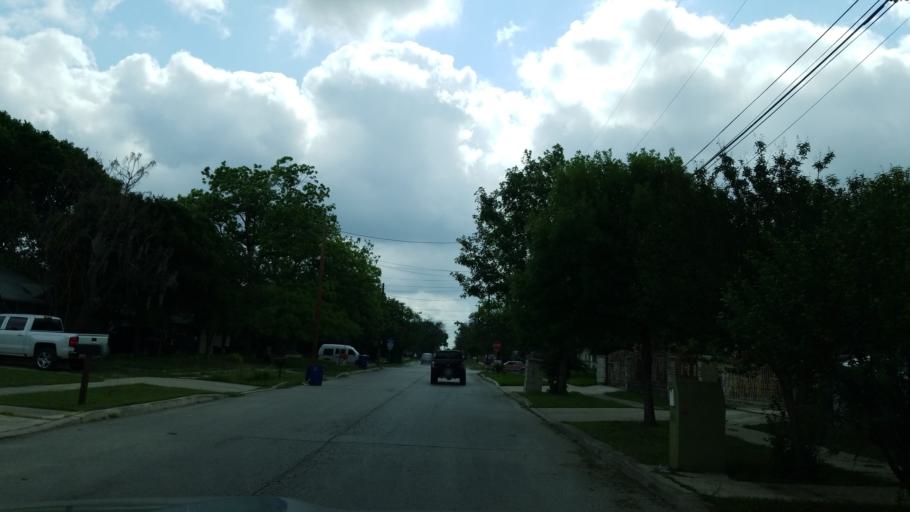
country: US
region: Texas
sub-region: Bexar County
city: San Antonio
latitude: 29.3578
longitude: -98.5240
